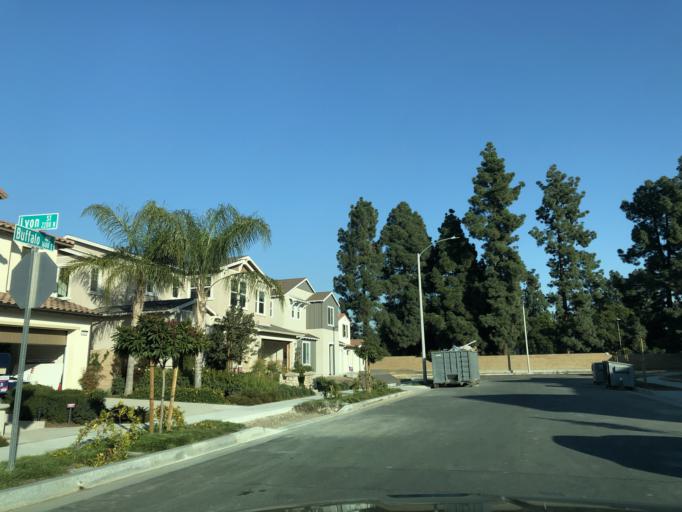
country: US
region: California
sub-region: Orange County
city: Orange
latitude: 33.7667
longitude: -117.8454
